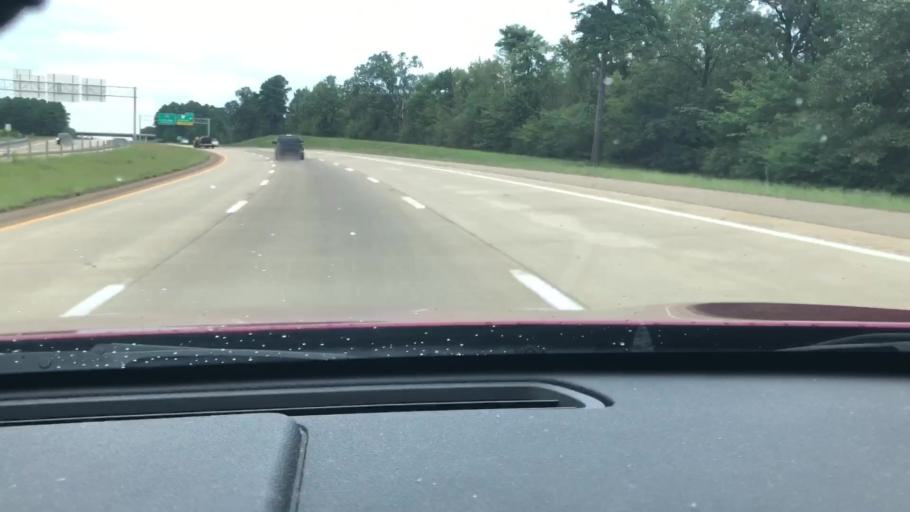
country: US
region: Texas
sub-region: Bowie County
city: Texarkana
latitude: 33.4045
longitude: -94.0049
